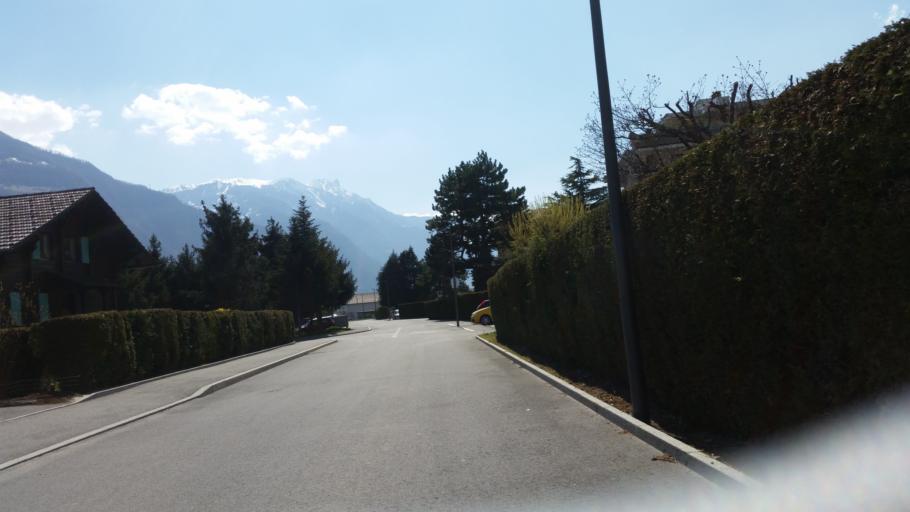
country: CH
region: Valais
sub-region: Conthey District
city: Ardon
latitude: 46.2069
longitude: 7.2554
